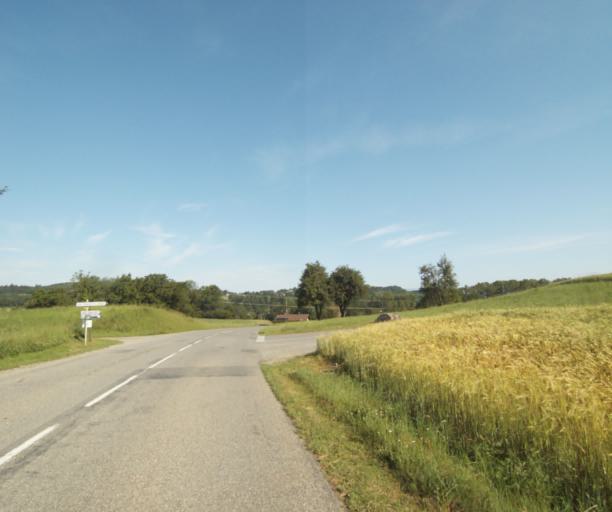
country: FR
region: Rhone-Alpes
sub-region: Departement de la Haute-Savoie
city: Allinges
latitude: 46.3183
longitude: 6.4792
